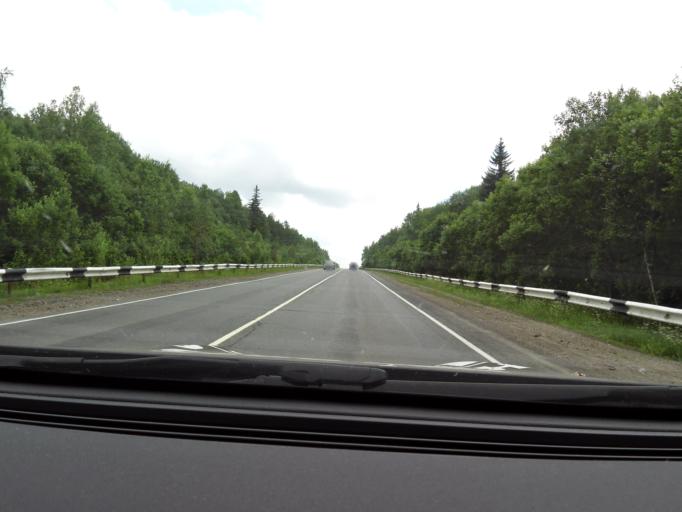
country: RU
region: Sverdlovsk
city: Achit
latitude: 56.8740
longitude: 57.6500
